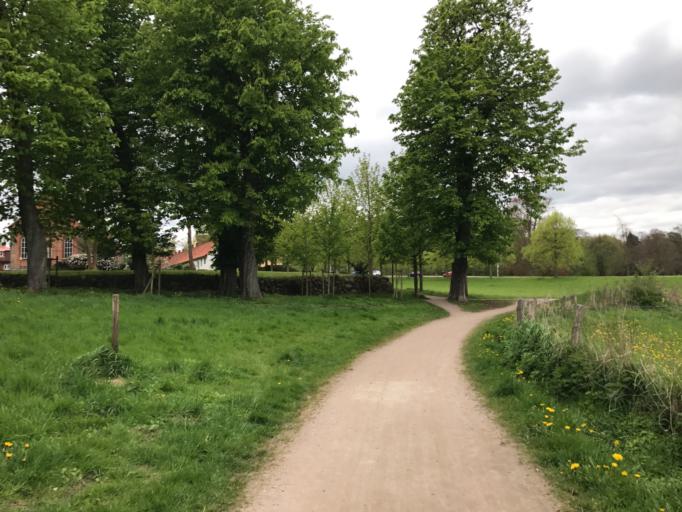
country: DE
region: Schleswig-Holstein
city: Ahrensburg
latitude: 53.6778
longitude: 10.2420
